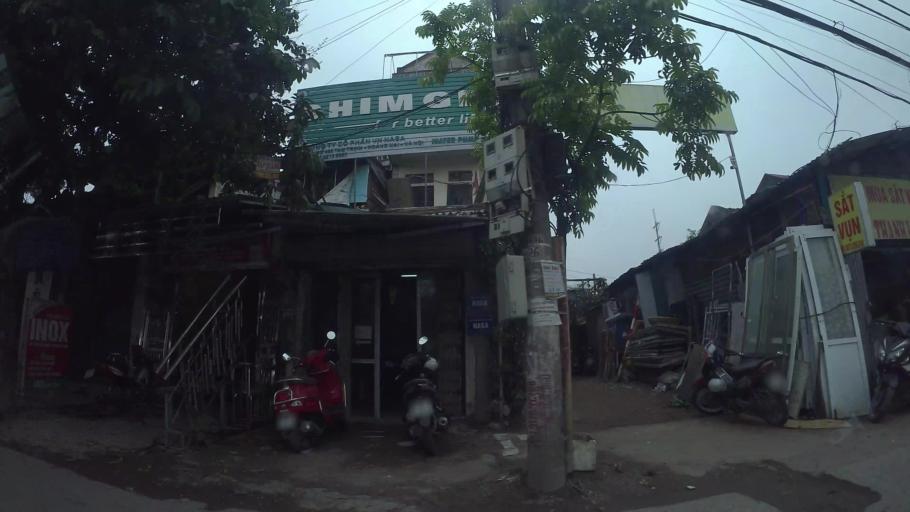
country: VN
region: Ha Noi
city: Hai BaTrung
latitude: 20.9830
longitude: 105.8640
